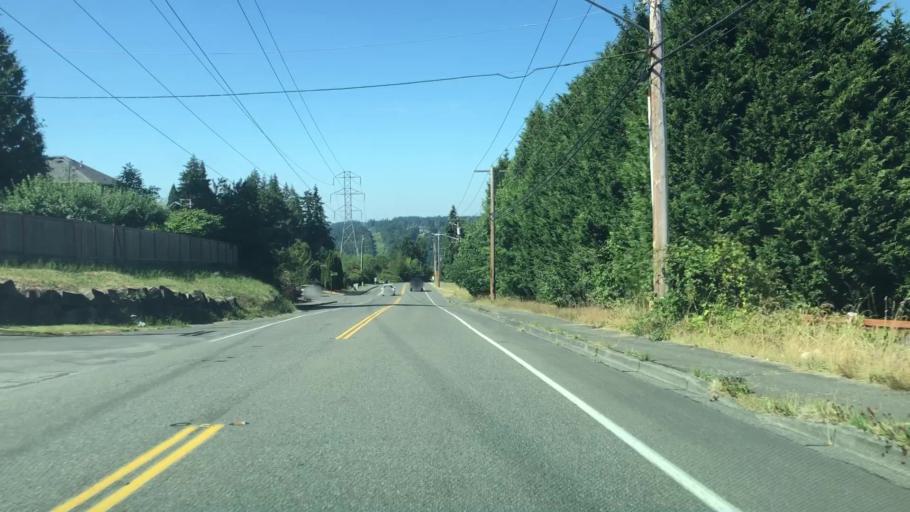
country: US
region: Washington
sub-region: King County
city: Woodinville
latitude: 47.7465
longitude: -122.1747
